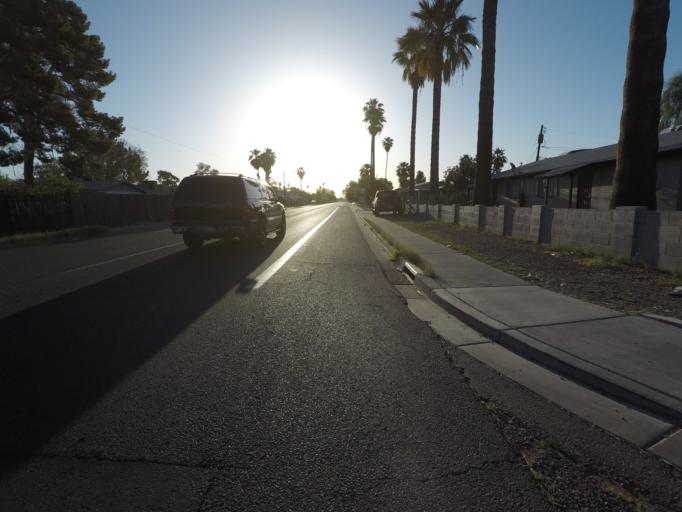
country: US
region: Arizona
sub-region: Maricopa County
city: Phoenix
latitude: 33.4730
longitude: -112.0204
